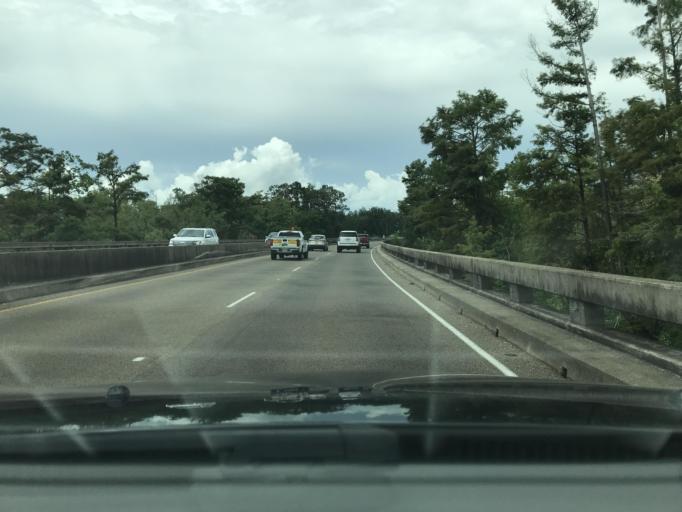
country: US
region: Louisiana
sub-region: Calcasieu Parish
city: Moss Bluff
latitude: 30.2948
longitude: -93.1942
